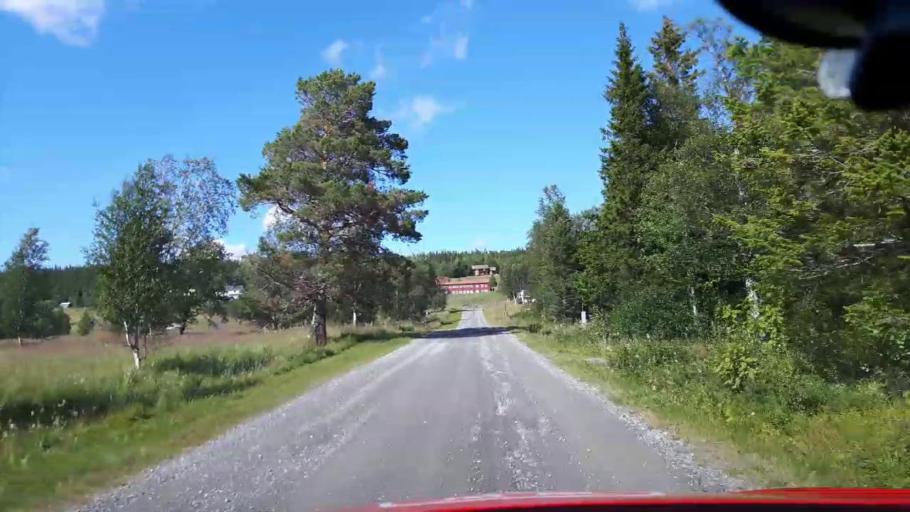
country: SE
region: Jaemtland
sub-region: Are Kommun
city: Are
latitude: 63.2124
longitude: 13.0538
